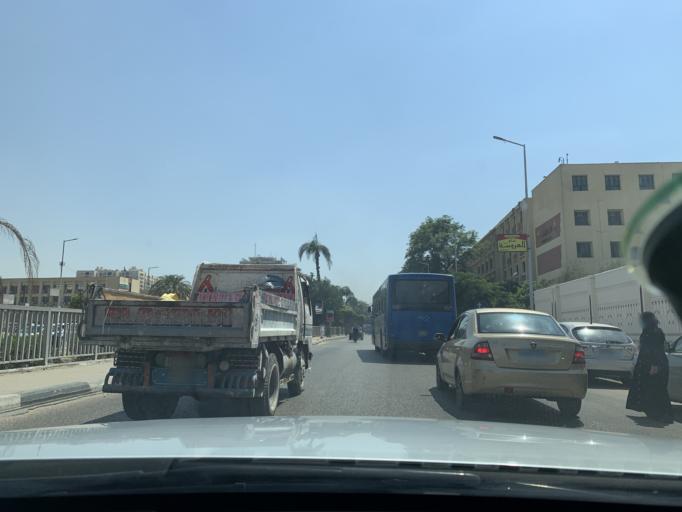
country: EG
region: Muhafazat al Qahirah
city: Cairo
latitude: 30.0772
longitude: 31.2884
